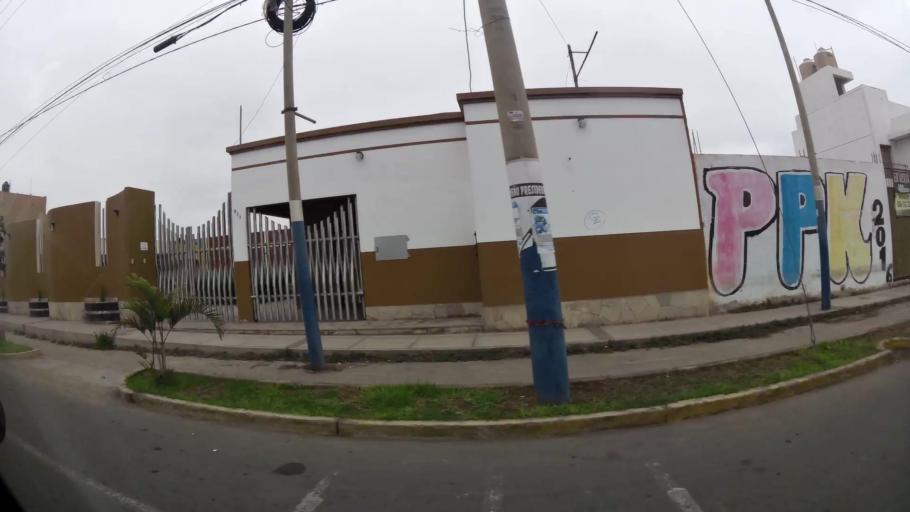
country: PE
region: Ica
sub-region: Provincia de Pisco
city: Pisco
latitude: -13.7096
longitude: -76.2127
